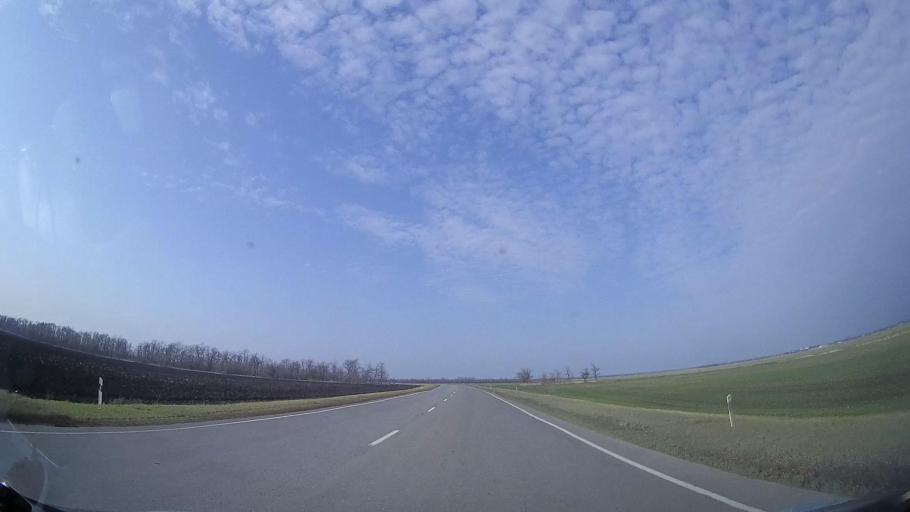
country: RU
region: Rostov
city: Tselina
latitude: 46.5140
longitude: 41.0418
